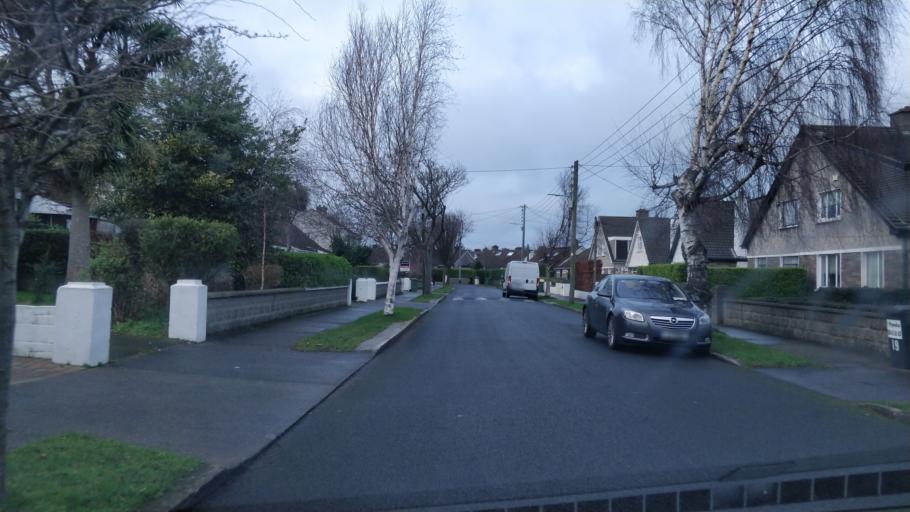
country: IE
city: Booterstown
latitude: 53.2858
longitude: -6.2000
